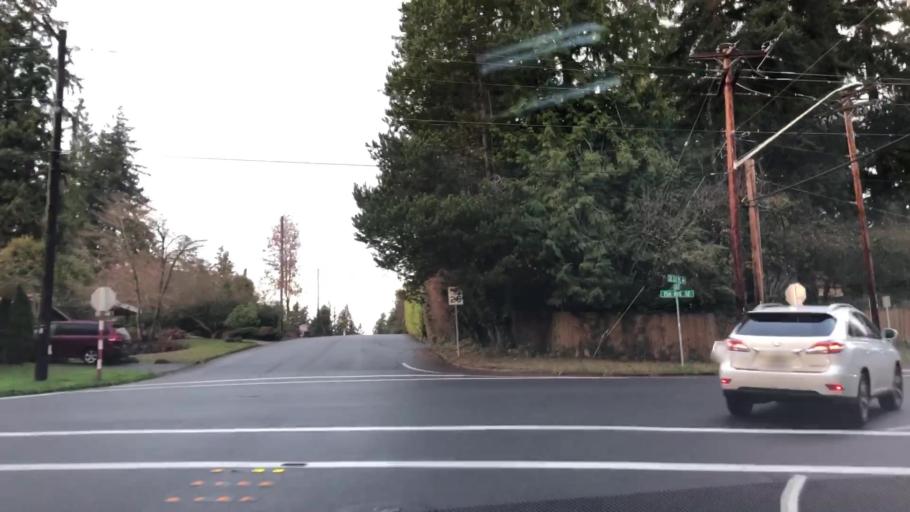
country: US
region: Washington
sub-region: King County
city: Eastgate
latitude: 47.5891
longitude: -122.1323
